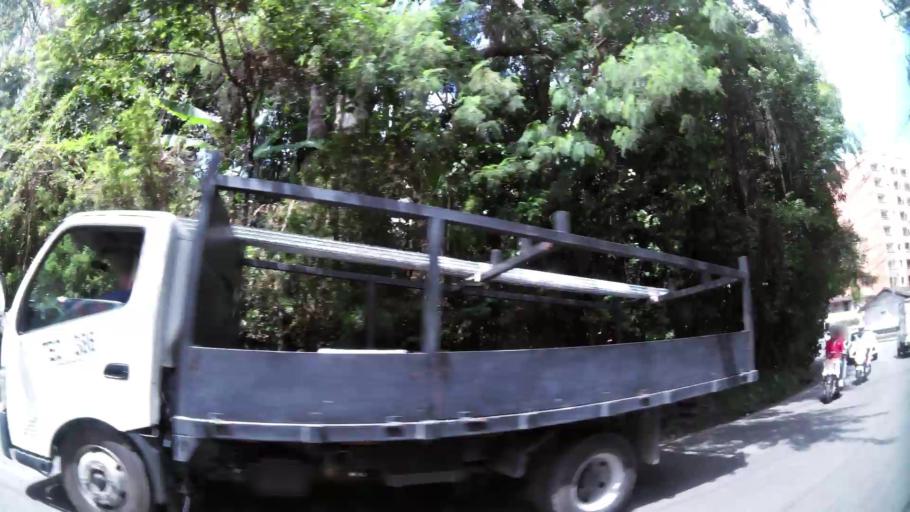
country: CO
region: Antioquia
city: Sabaneta
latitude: 6.1470
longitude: -75.6201
